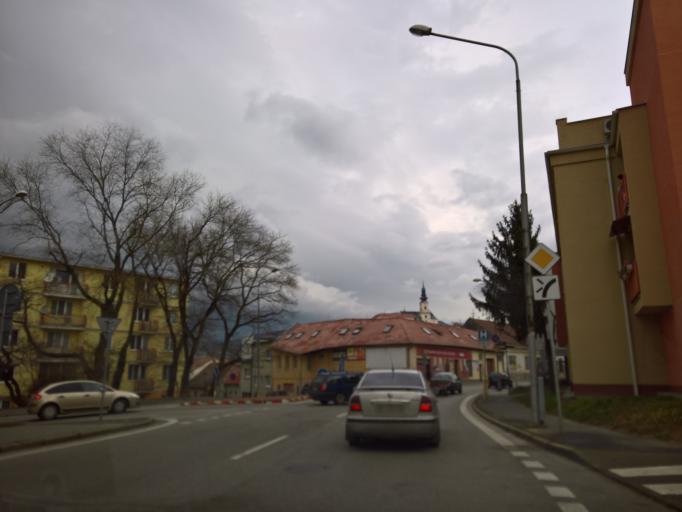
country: SK
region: Nitriansky
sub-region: Okres Nitra
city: Nitra
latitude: 48.3141
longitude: 18.0837
